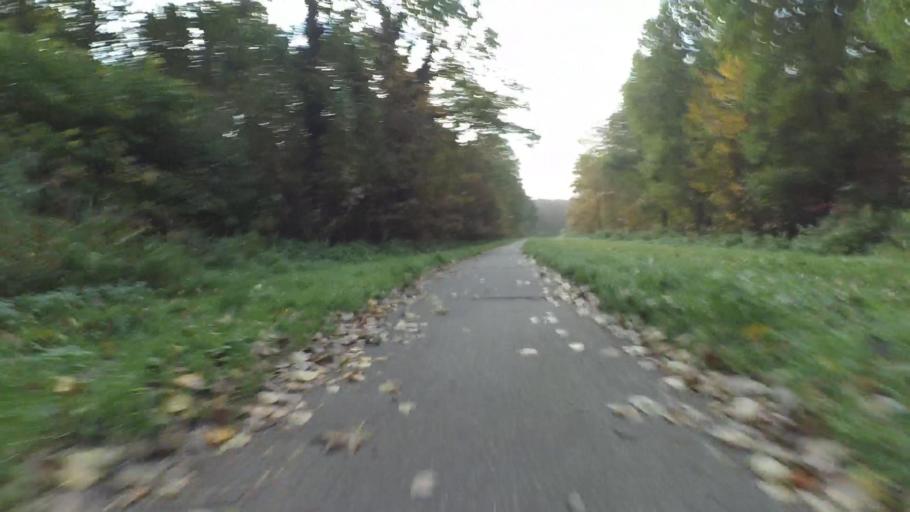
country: NL
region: North Holland
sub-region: Gemeente Huizen
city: Huizen
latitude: 52.3249
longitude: 5.2967
